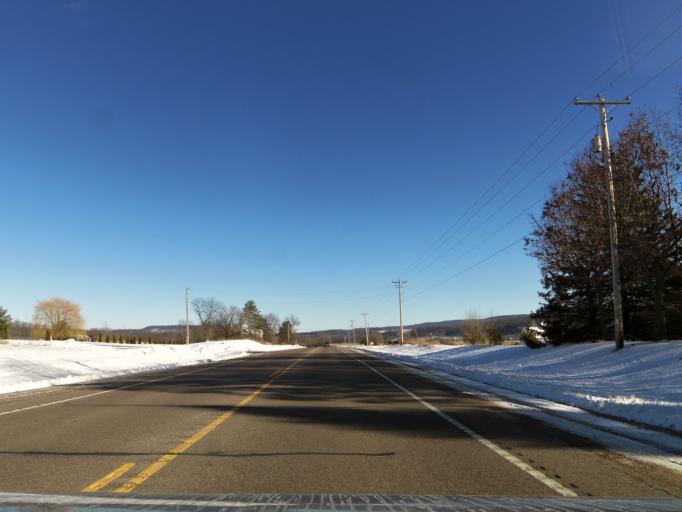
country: US
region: Wisconsin
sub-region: Sauk County
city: Baraboo
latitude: 43.4743
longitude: -89.6655
